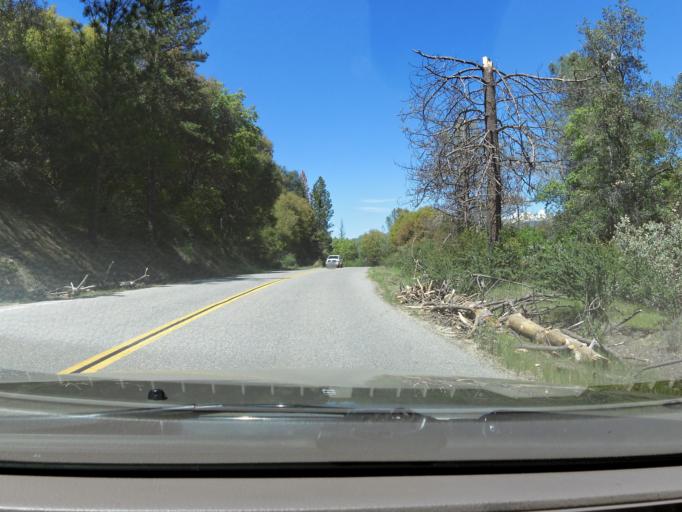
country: US
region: California
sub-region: Fresno County
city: Auberry
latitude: 37.2373
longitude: -119.5169
